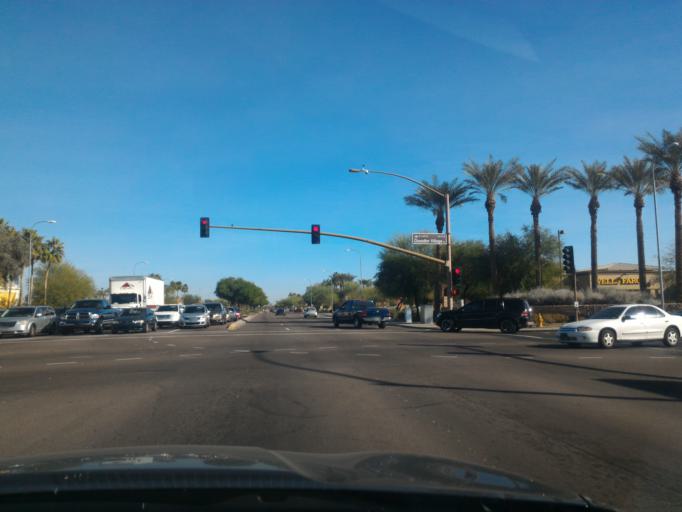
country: US
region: Arizona
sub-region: Maricopa County
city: Chandler
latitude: 33.3055
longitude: -111.9031
